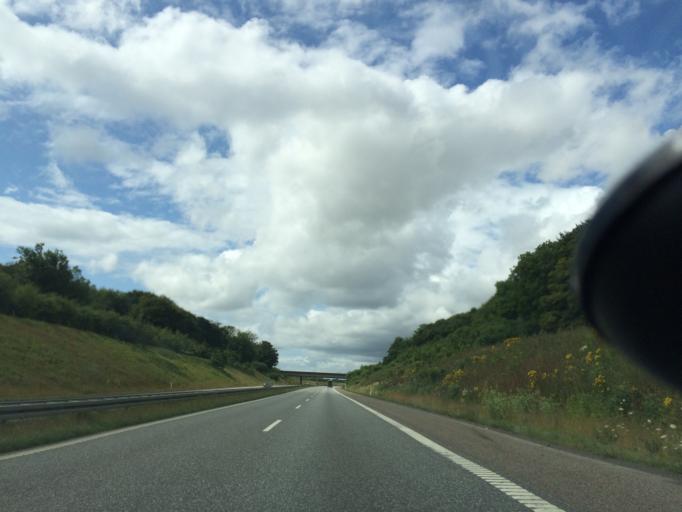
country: DK
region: Central Jutland
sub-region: Skanderborg Kommune
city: Skovby
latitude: 56.1475
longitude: 9.9671
